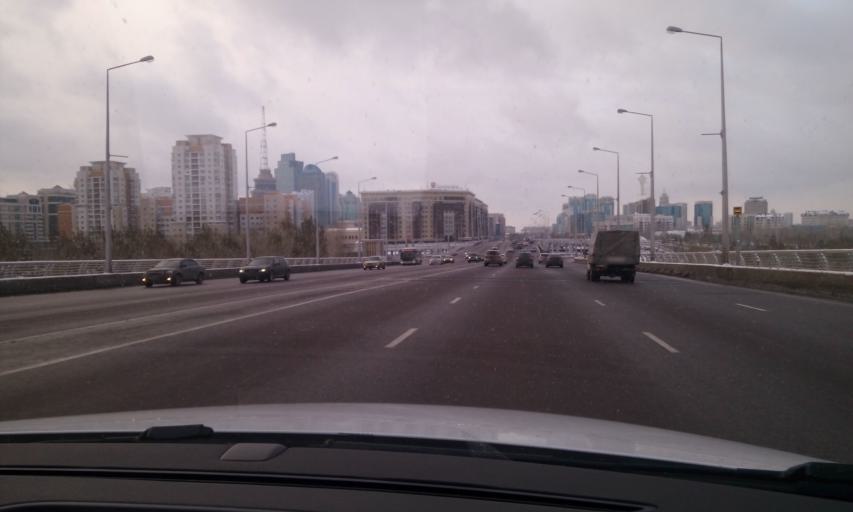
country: KZ
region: Astana Qalasy
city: Astana
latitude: 51.1316
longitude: 71.4455
